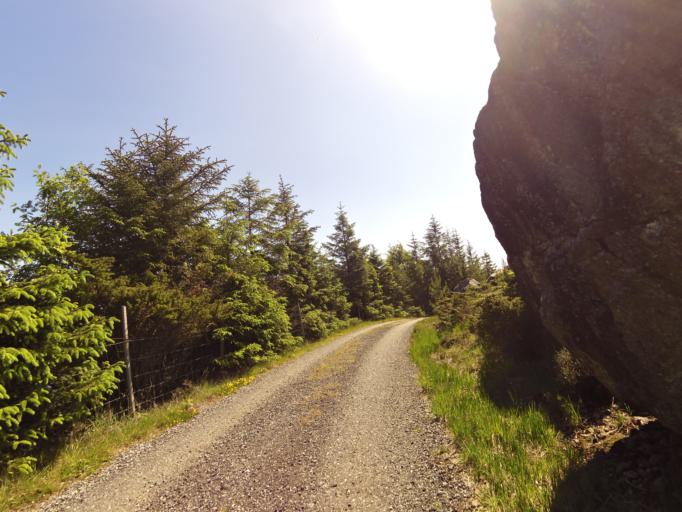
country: NO
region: Rogaland
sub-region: Eigersund
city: Egersund
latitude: 58.5043
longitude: 5.8943
